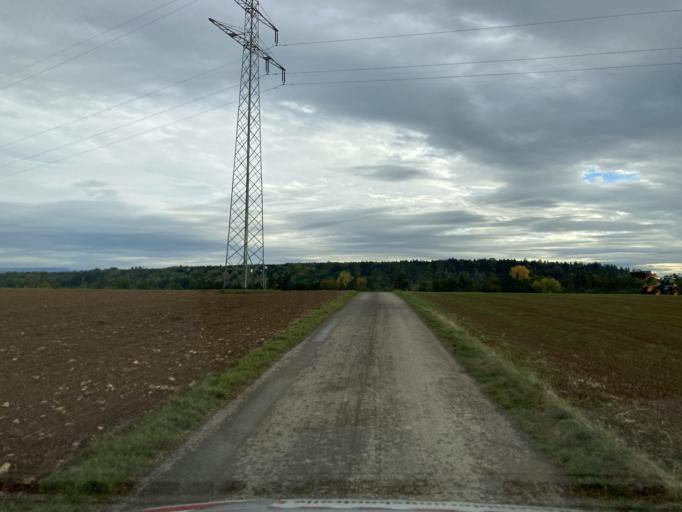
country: DE
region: Baden-Wuerttemberg
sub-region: Regierungsbezirk Stuttgart
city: Bondorf
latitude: 48.4974
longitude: 8.8590
